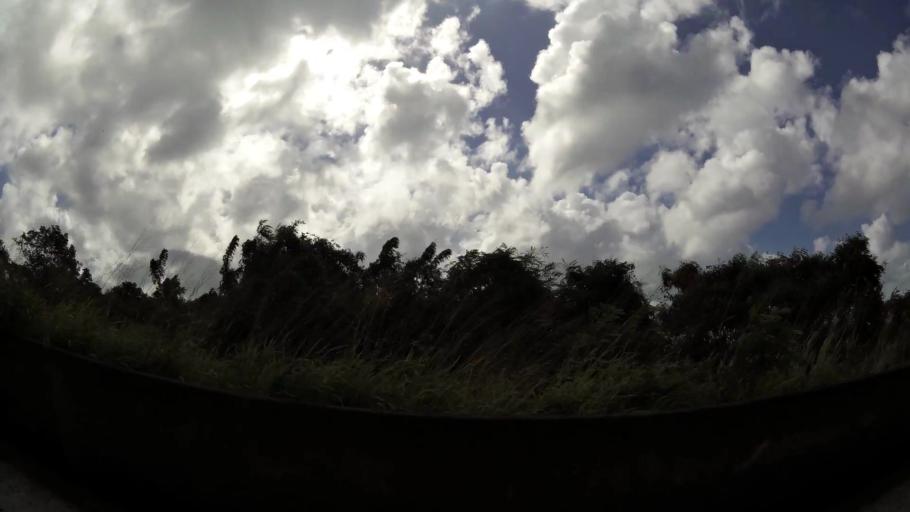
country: MQ
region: Martinique
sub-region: Martinique
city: Les Trois-Ilets
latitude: 14.4818
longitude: -61.0035
